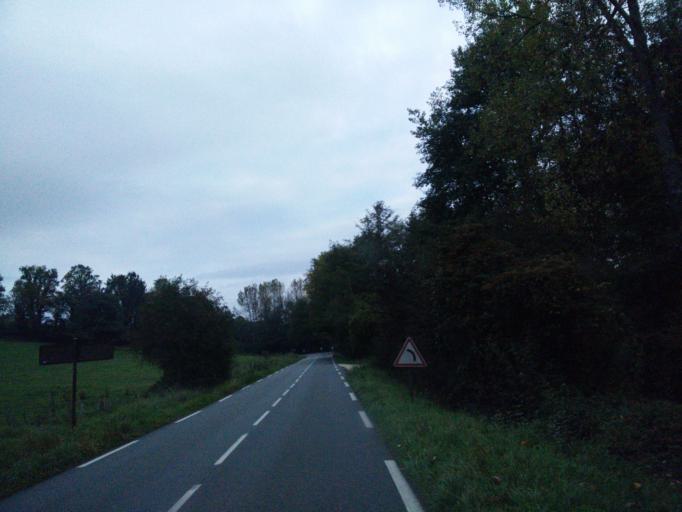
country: FR
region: Aquitaine
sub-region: Departement de la Dordogne
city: Carsac-Aillac
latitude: 44.7994
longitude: 1.3026
